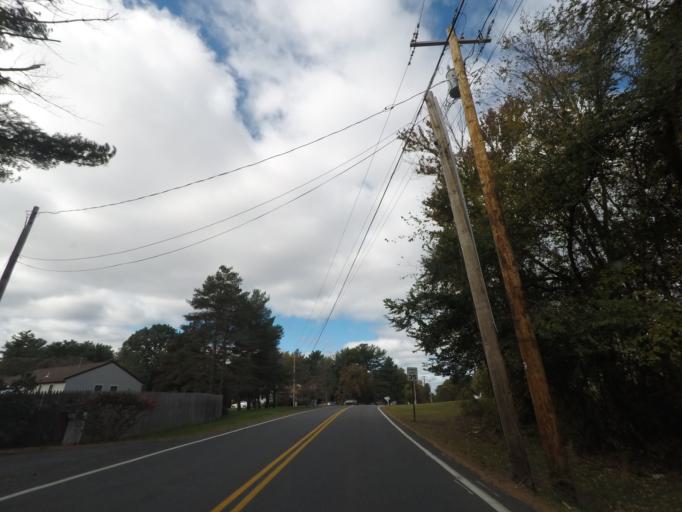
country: US
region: New York
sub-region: Albany County
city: Cohoes
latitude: 42.8318
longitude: -73.7567
